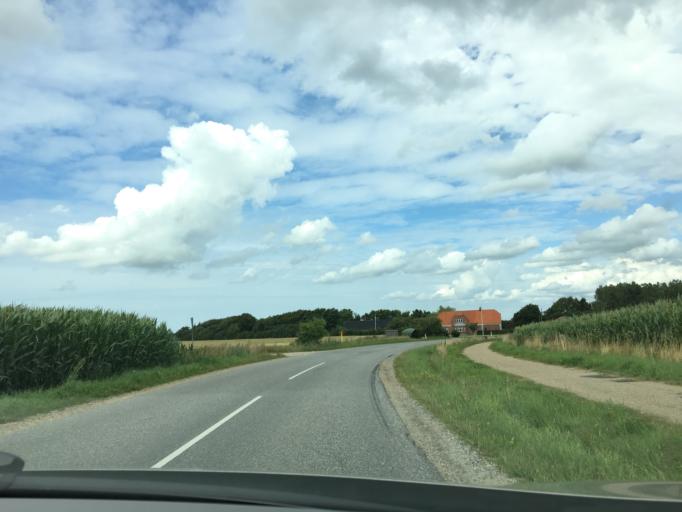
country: DK
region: South Denmark
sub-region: Varde Kommune
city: Oksbol
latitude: 55.6606
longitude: 8.2932
